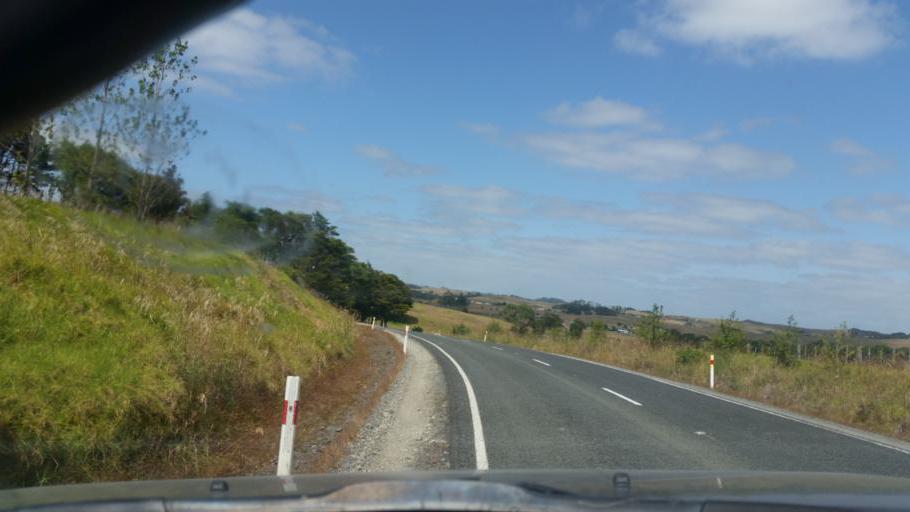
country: NZ
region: Northland
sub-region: Whangarei
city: Ruakaka
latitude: -35.9580
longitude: 174.2929
